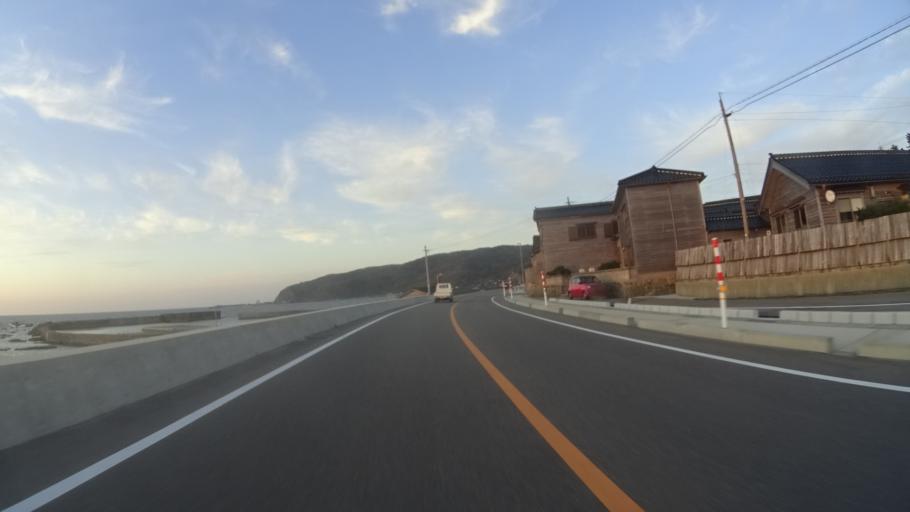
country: JP
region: Ishikawa
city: Nanao
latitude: 37.2809
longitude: 136.7336
